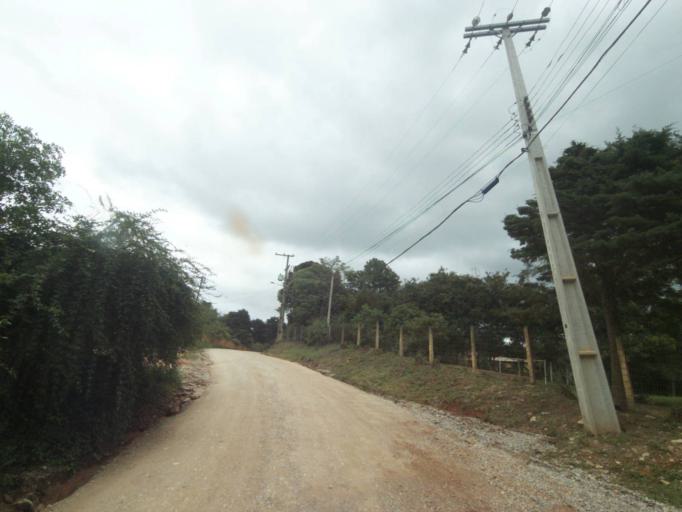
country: BR
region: Parana
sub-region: Campina Grande Do Sul
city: Campina Grande do Sul
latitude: -25.3215
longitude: -49.0805
